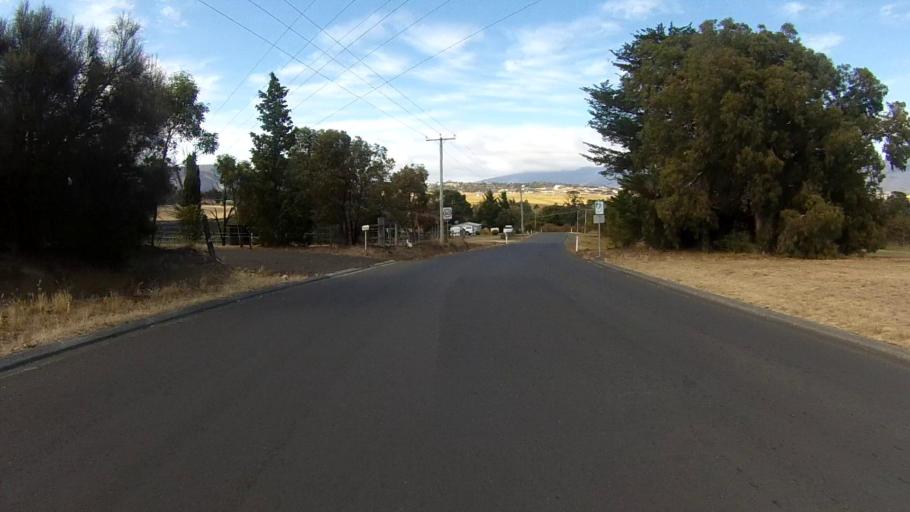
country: AU
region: Tasmania
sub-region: Brighton
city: Old Beach
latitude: -42.7509
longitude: 147.2796
